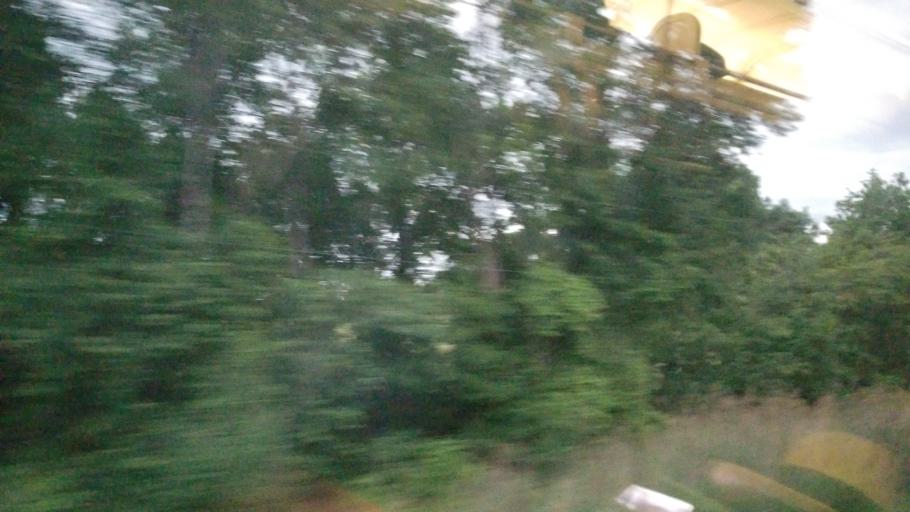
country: US
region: Virginia
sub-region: Orange County
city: Orange
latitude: 38.2535
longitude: -78.1088
